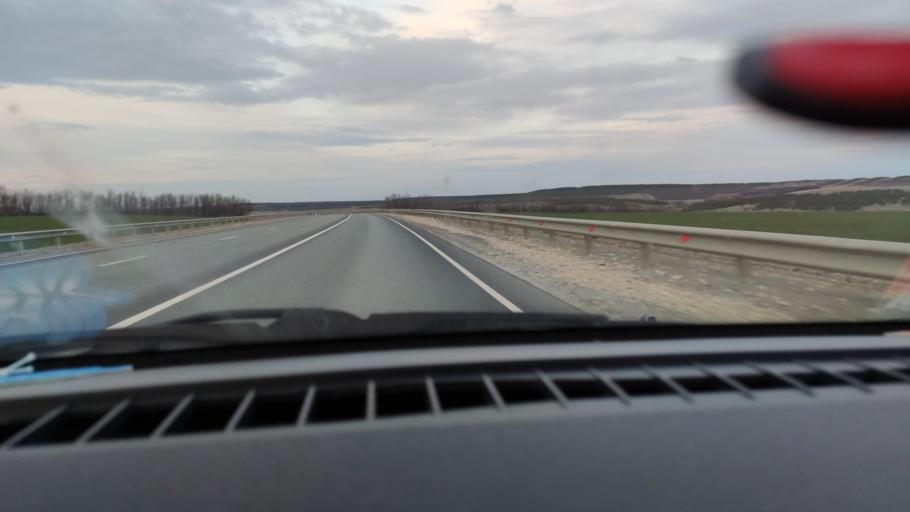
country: RU
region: Saratov
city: Yelshanka
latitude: 51.8390
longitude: 46.4768
